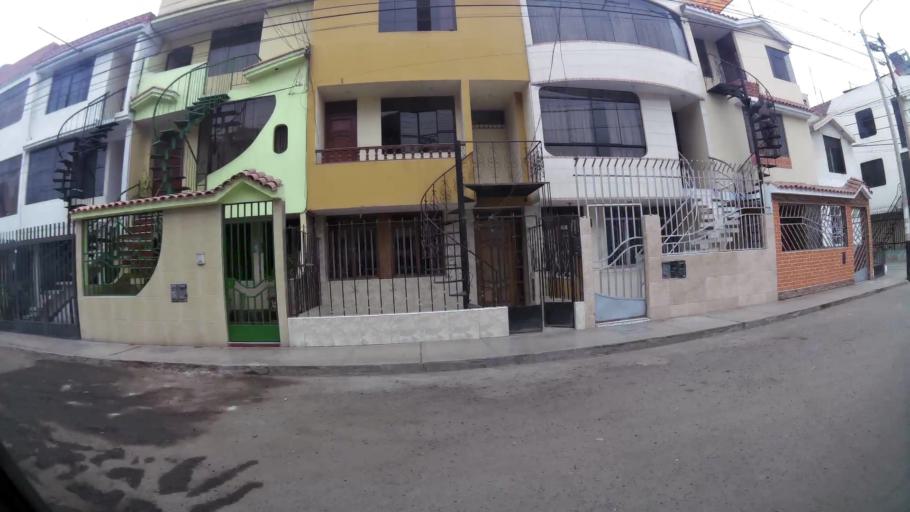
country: PE
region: La Libertad
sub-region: Provincia de Trujillo
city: Trujillo
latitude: -8.1249
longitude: -79.0341
